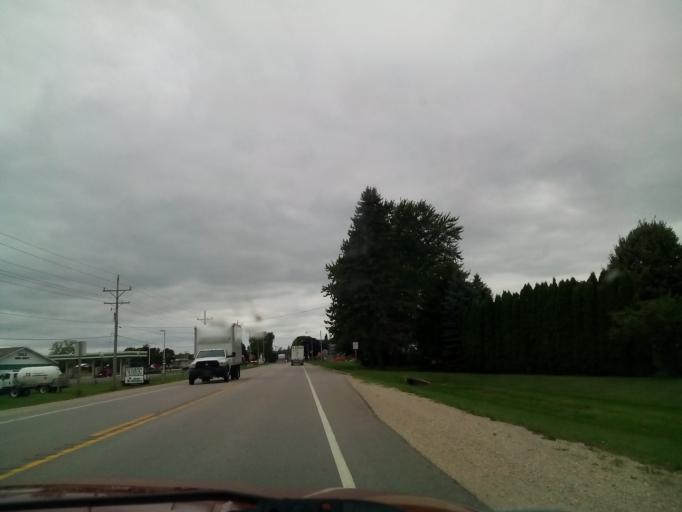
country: US
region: Wisconsin
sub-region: Outagamie County
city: Hortonville
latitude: 44.2730
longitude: -88.6710
